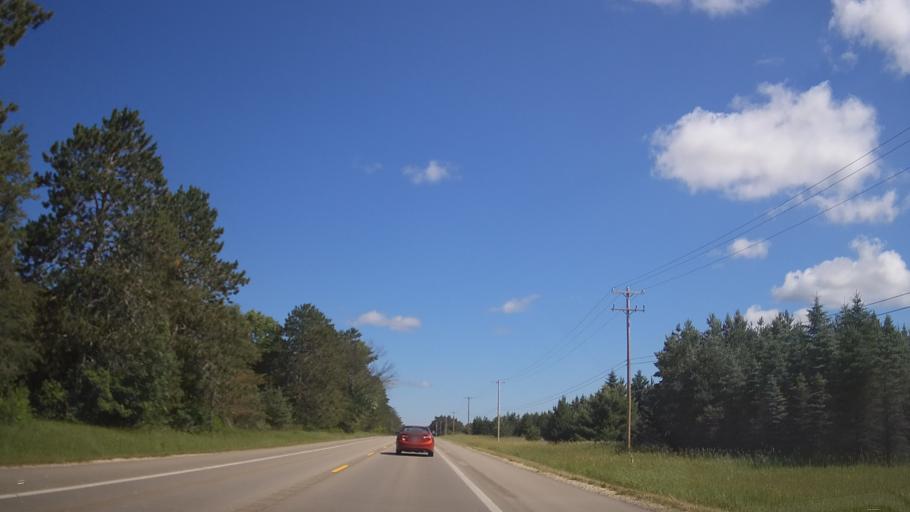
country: US
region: Michigan
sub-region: Cheboygan County
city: Indian River
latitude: 45.4806
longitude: -84.7811
